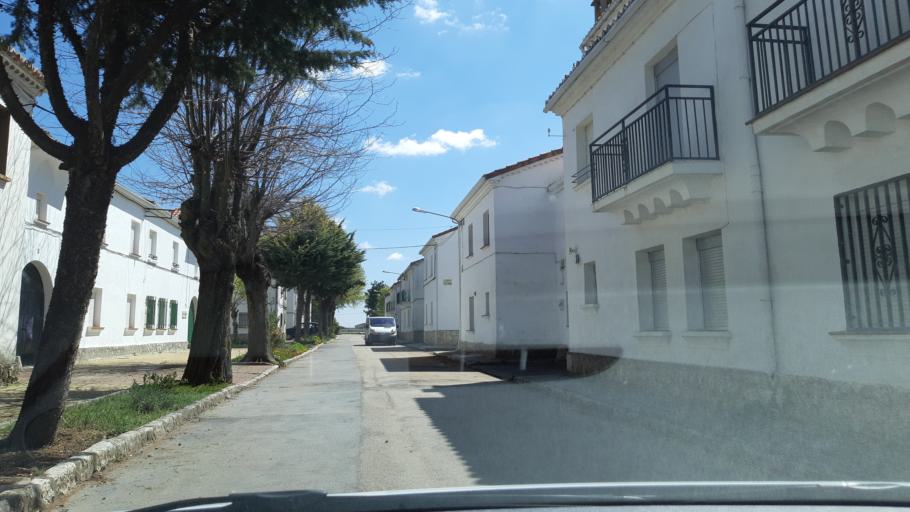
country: ES
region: Castille-La Mancha
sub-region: Provincia de Guadalajara
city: Gajanejos
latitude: 40.8418
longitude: -2.8923
